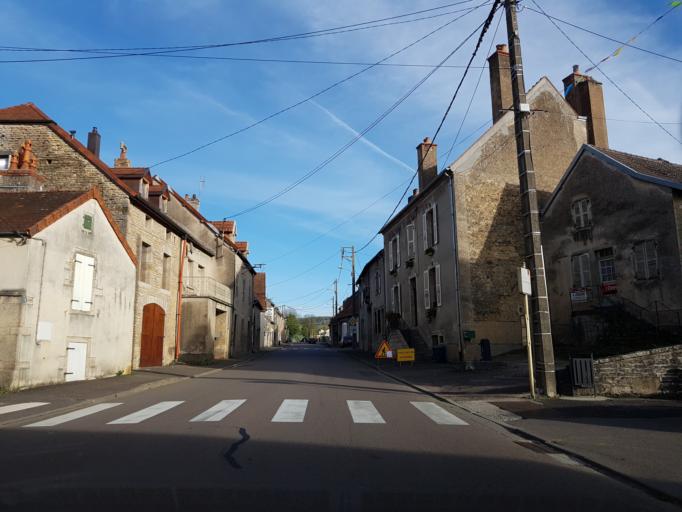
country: FR
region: Bourgogne
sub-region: Departement de la Cote-d'Or
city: Vitteaux
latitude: 47.3960
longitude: 4.5438
